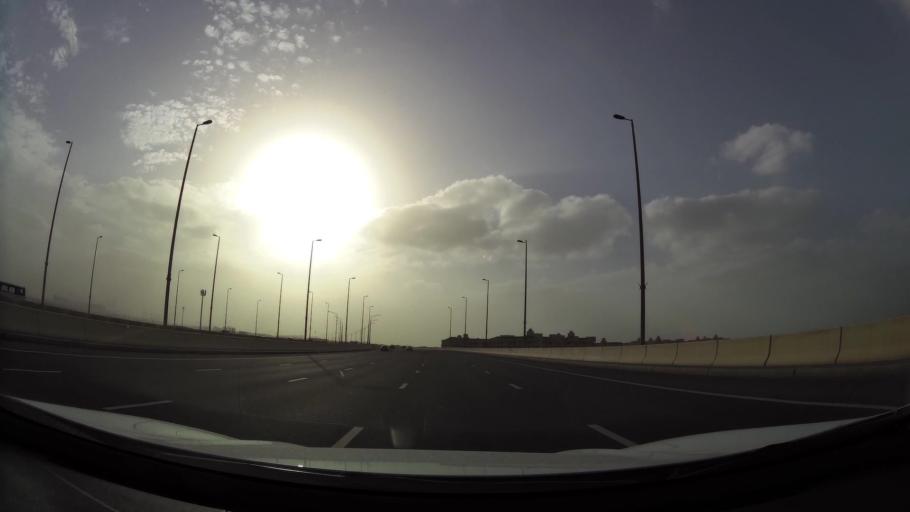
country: AE
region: Abu Dhabi
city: Abu Dhabi
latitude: 24.5495
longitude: 54.4571
